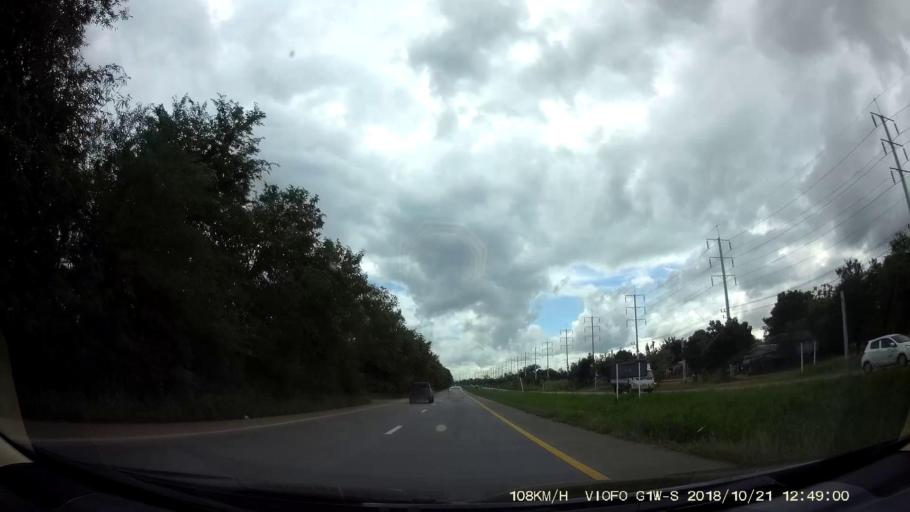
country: TH
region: Nakhon Ratchasima
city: Amphoe Sikhiu
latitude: 14.9032
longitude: 101.6841
